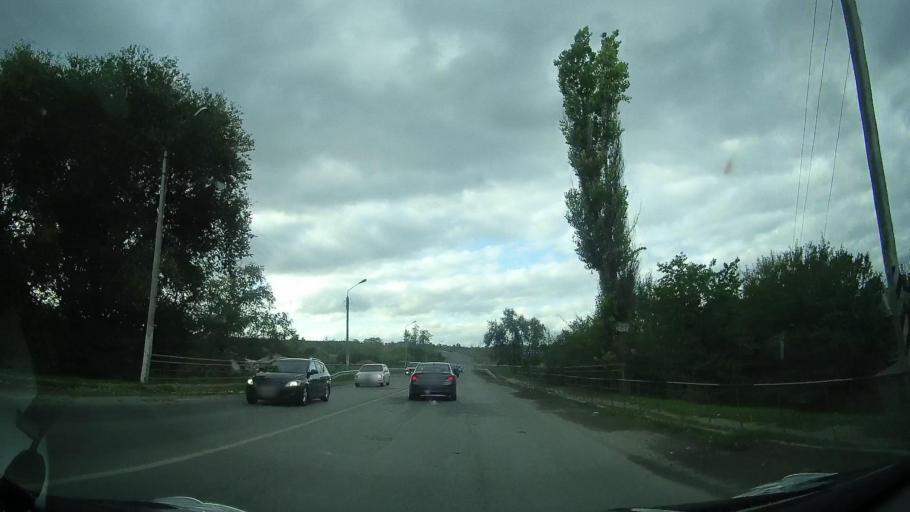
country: RU
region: Rostov
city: Kagal'nitskaya
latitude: 46.8847
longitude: 40.1452
